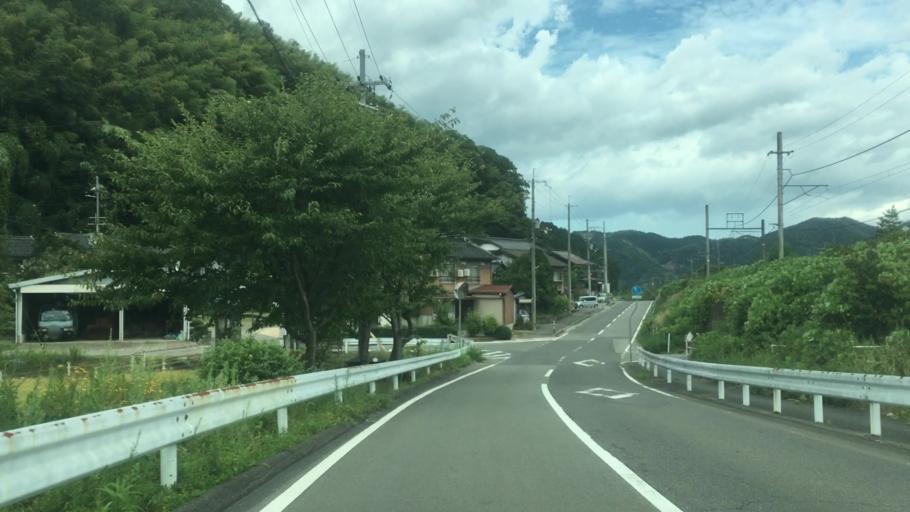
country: JP
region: Hyogo
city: Toyooka
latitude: 35.5658
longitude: 134.8034
